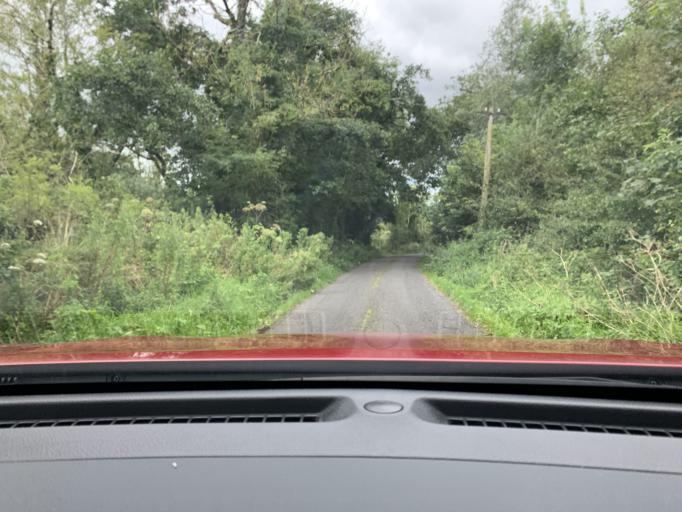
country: IE
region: Connaught
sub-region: Sligo
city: Collooney
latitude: 54.1641
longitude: -8.4291
